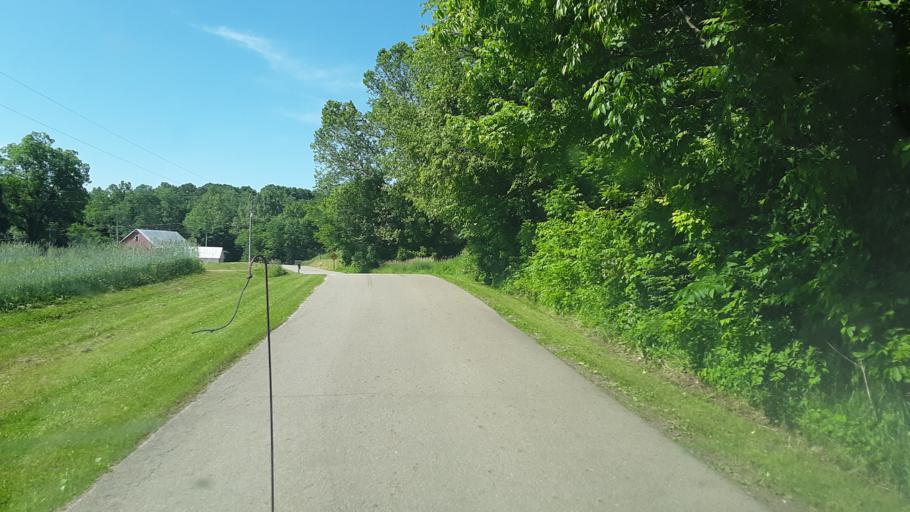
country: US
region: Ohio
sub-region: Tuscarawas County
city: Newcomerstown
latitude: 40.2272
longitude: -81.6708
